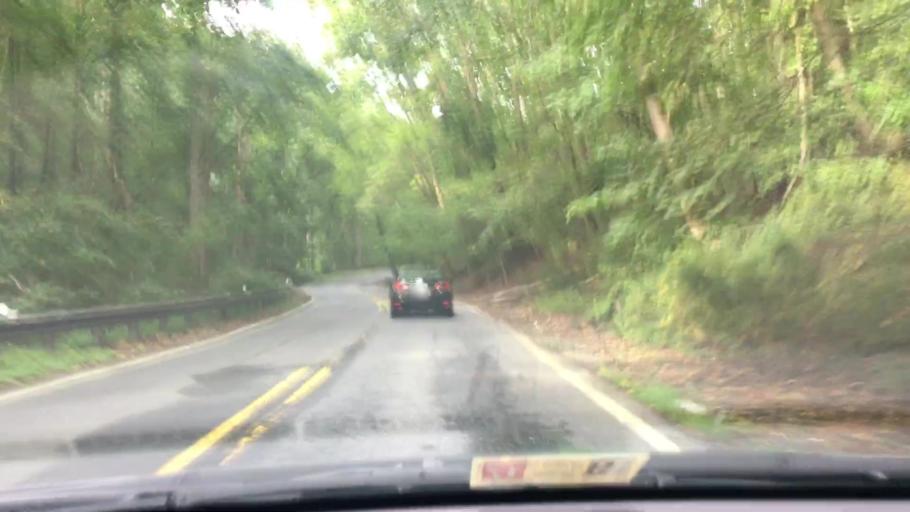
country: US
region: Maryland
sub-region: Montgomery County
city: Cabin John
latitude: 38.9955
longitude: -77.1700
